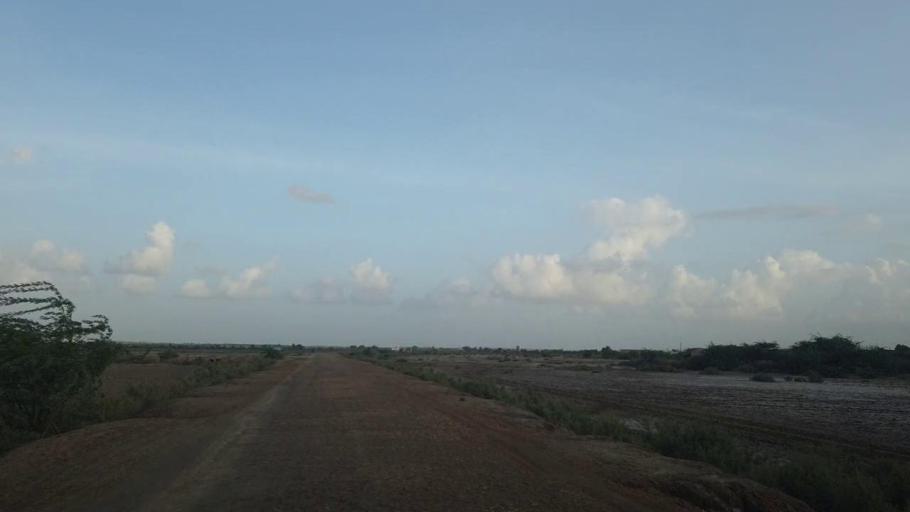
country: PK
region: Sindh
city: Kadhan
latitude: 24.5561
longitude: 69.1223
